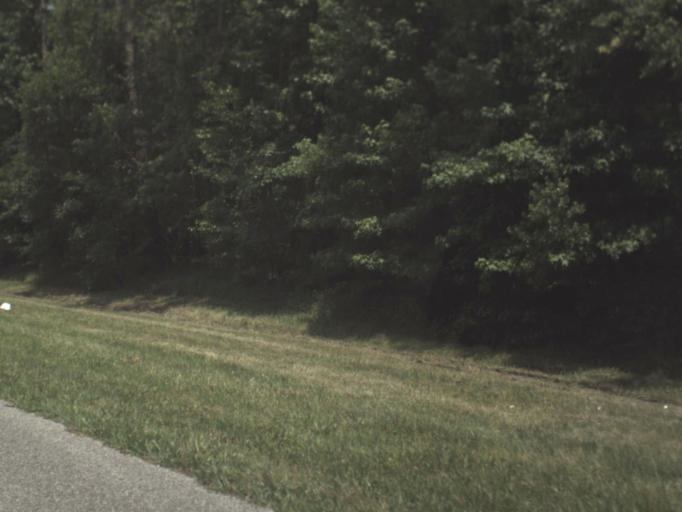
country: US
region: Florida
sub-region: Alachua County
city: Gainesville
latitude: 29.7099
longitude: -82.2722
